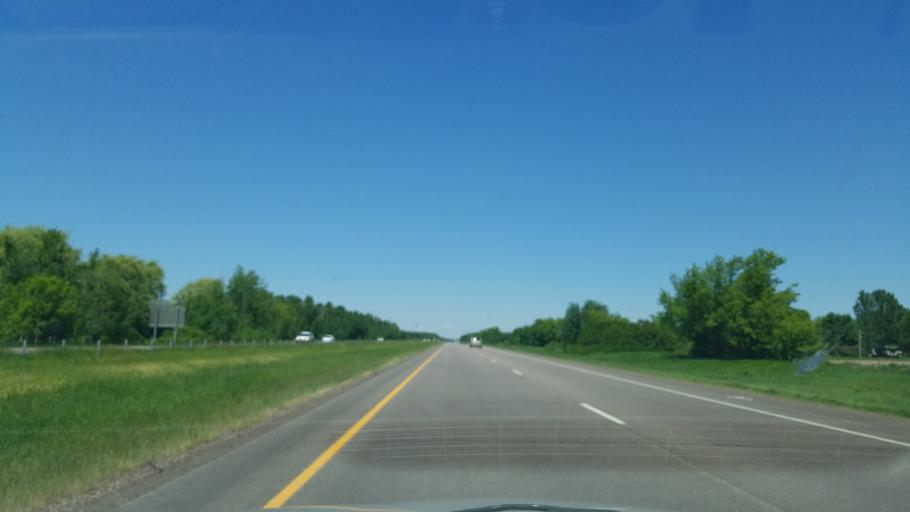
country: US
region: Minnesota
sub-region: Chisago County
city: Rush City
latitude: 45.7002
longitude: -92.9922
